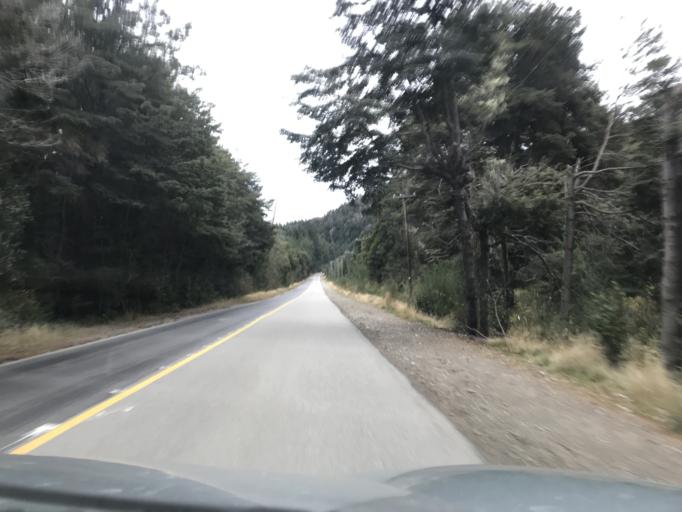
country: AR
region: Rio Negro
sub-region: Departamento de Bariloche
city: San Carlos de Bariloche
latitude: -41.0834
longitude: -71.5449
